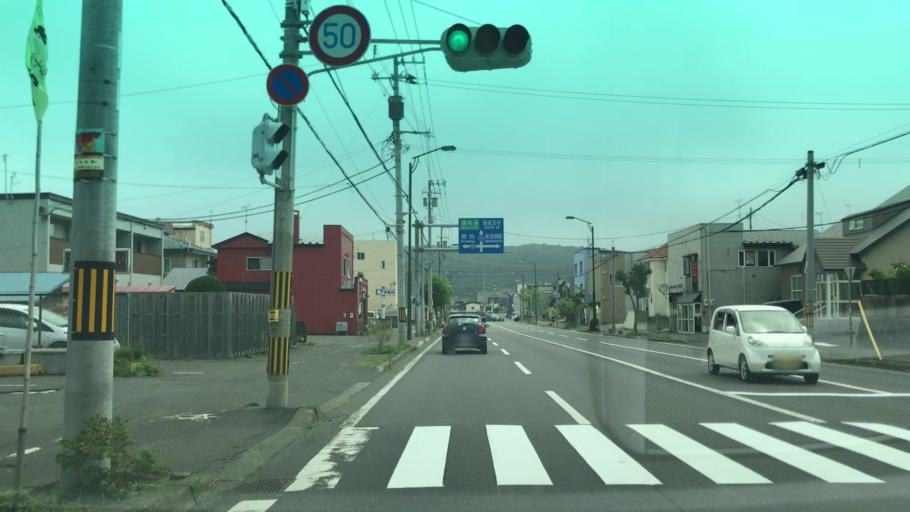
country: JP
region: Hokkaido
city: Muroran
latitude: 42.3621
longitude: 141.0401
